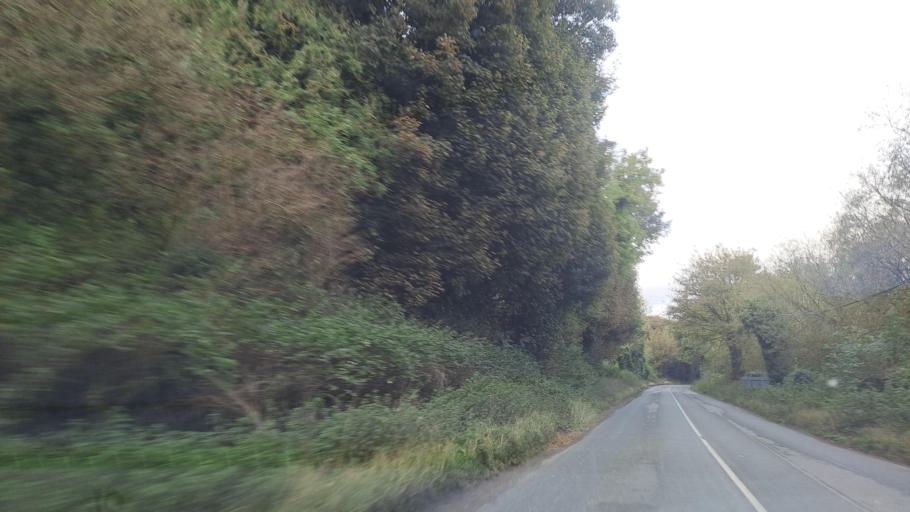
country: IE
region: Ulster
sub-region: An Cabhan
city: Kingscourt
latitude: 53.8776
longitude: -6.8058
